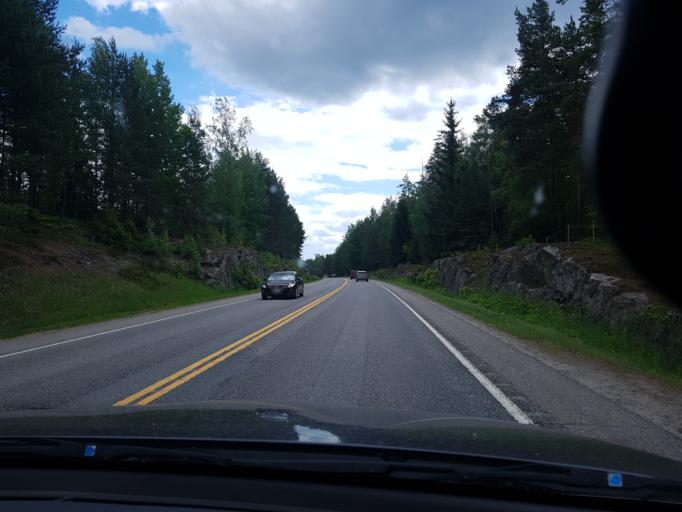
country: FI
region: Pirkanmaa
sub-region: Tampere
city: Paelkaene
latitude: 61.3144
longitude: 24.2858
